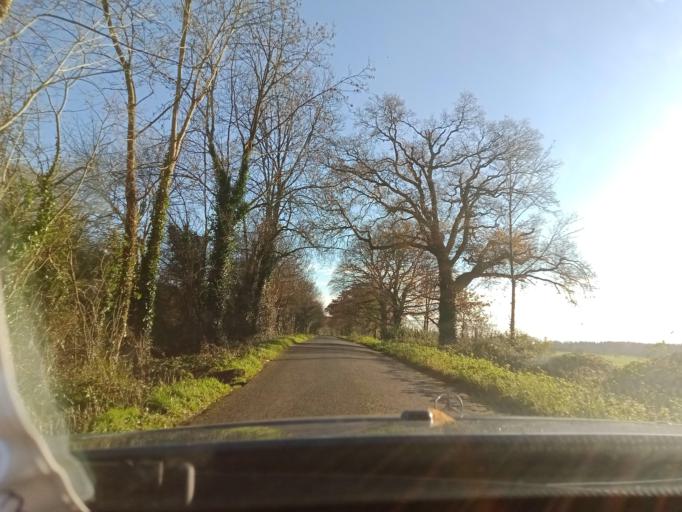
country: IE
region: Leinster
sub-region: Kilkenny
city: Piltown
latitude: 52.3515
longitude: -7.2877
